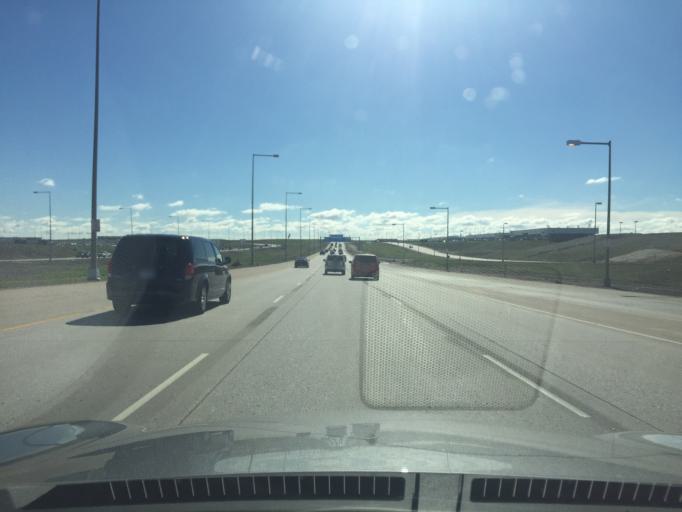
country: US
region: Colorado
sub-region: Weld County
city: Lochbuie
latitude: 39.8335
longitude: -104.6873
